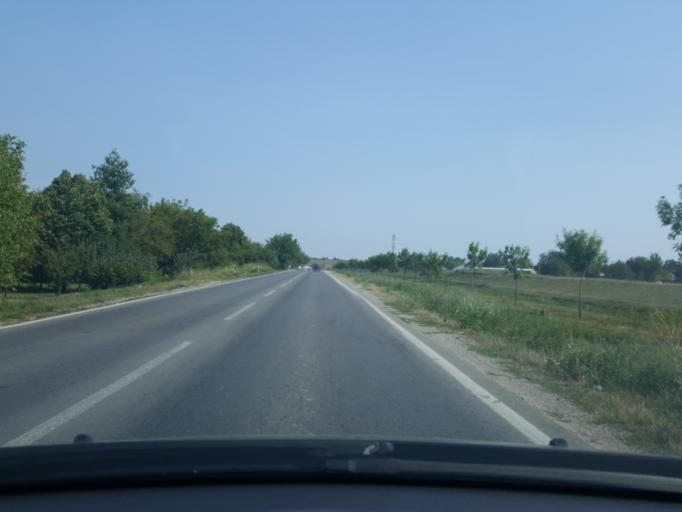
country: RS
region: Central Serbia
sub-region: Macvanski Okrug
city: Sabac
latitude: 44.7441
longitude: 19.6696
